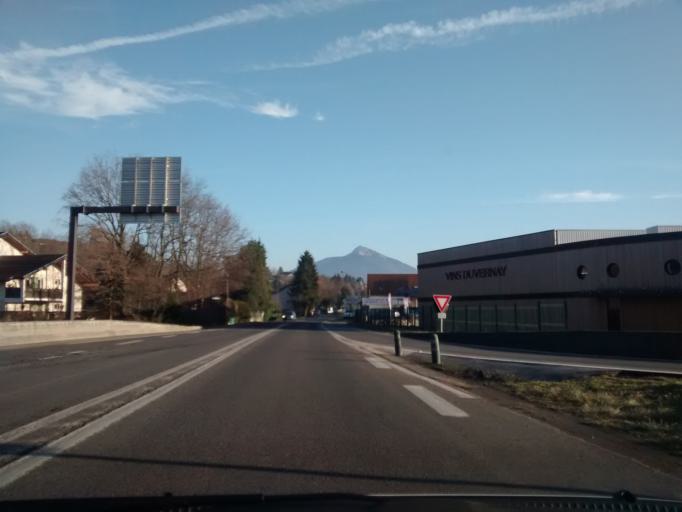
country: FR
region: Rhone-Alpes
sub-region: Departement de la Haute-Savoie
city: Bonne-sur-Menoge
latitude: 46.1728
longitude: 6.3115
